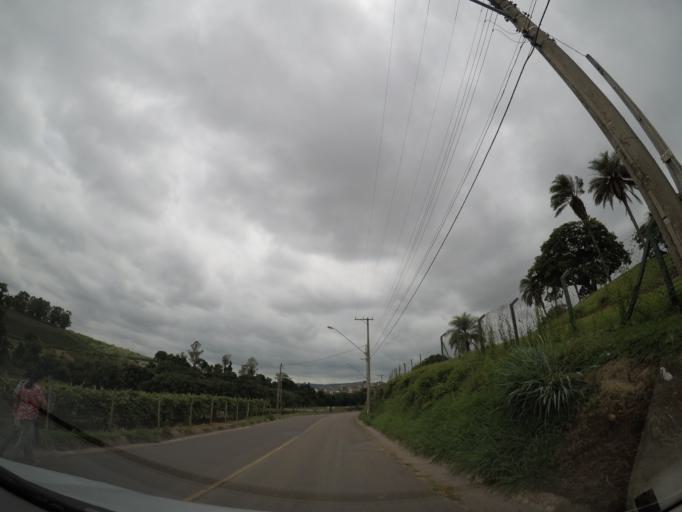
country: BR
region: Sao Paulo
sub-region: Louveira
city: Louveira
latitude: -23.0958
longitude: -46.9875
